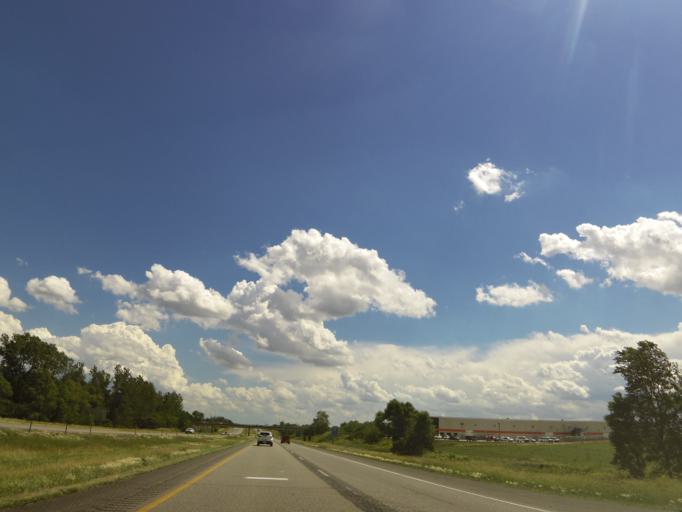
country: US
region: Iowa
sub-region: Linn County
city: Ely
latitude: 41.8797
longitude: -91.6706
